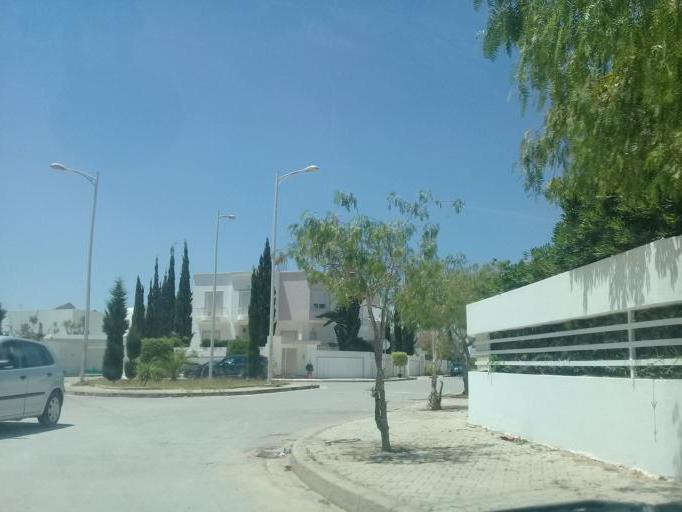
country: TN
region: Tunis
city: La Goulette
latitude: 36.8429
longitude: 10.2725
